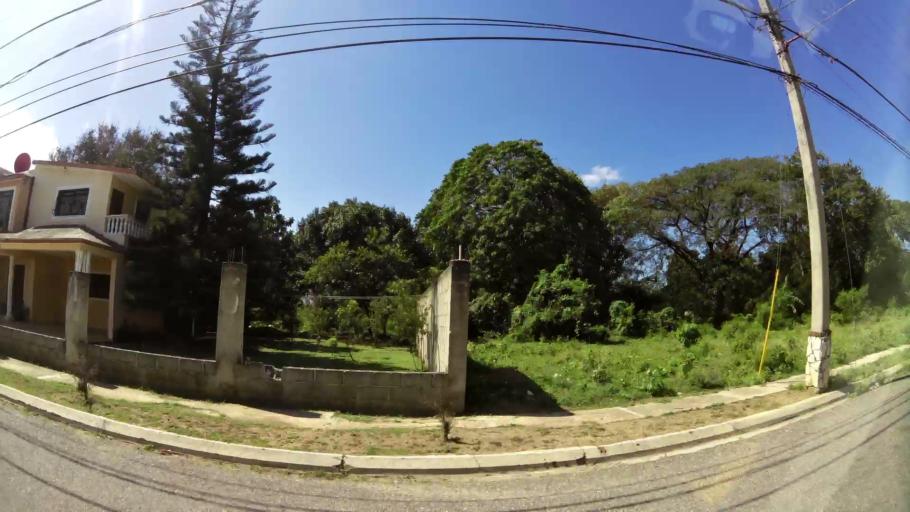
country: DO
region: San Cristobal
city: San Cristobal
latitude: 18.4338
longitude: -70.1281
